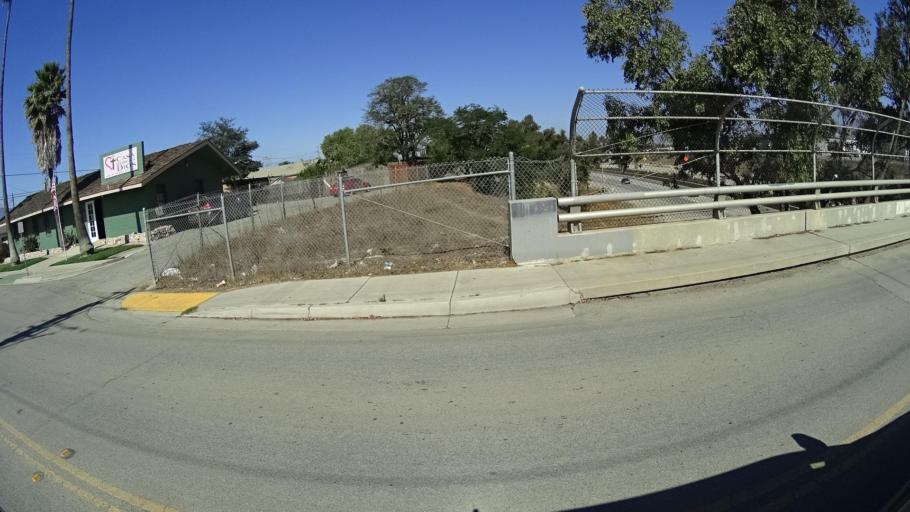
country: US
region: California
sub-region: Monterey County
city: Greenfield
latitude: 36.3204
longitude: -121.2362
